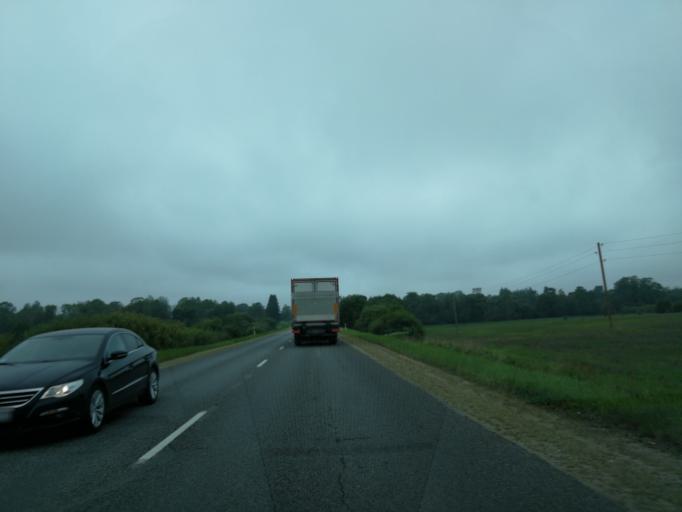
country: LV
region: Livani
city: Livani
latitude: 56.3416
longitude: 26.3514
